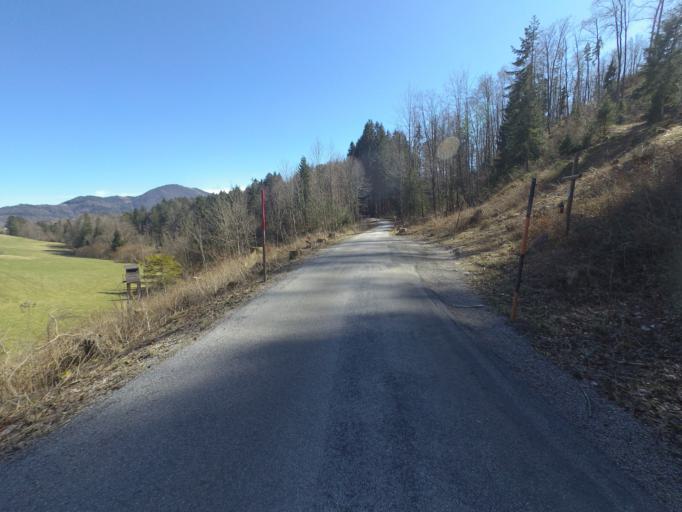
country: AT
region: Salzburg
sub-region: Politischer Bezirk Salzburg-Umgebung
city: Koppl
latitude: 47.8003
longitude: 13.1500
